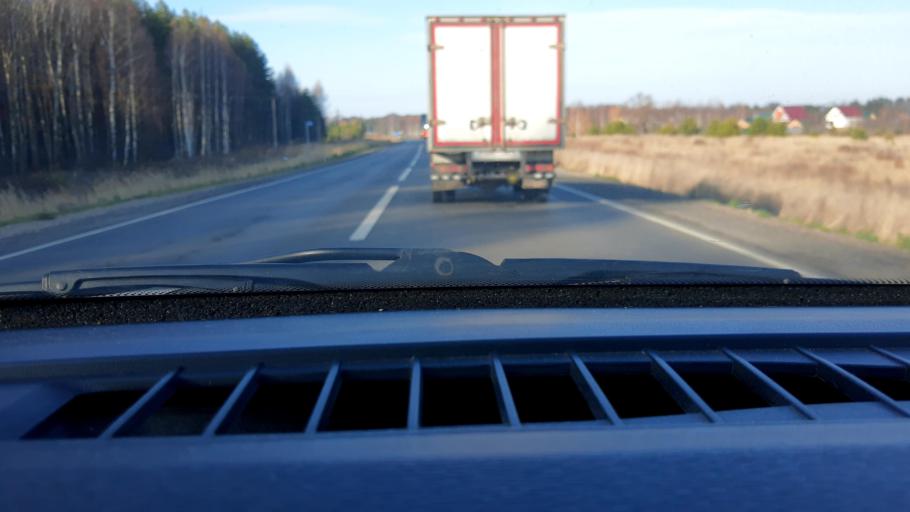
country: RU
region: Nizjnij Novgorod
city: Novaya Balakhna
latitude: 56.6094
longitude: 43.6079
